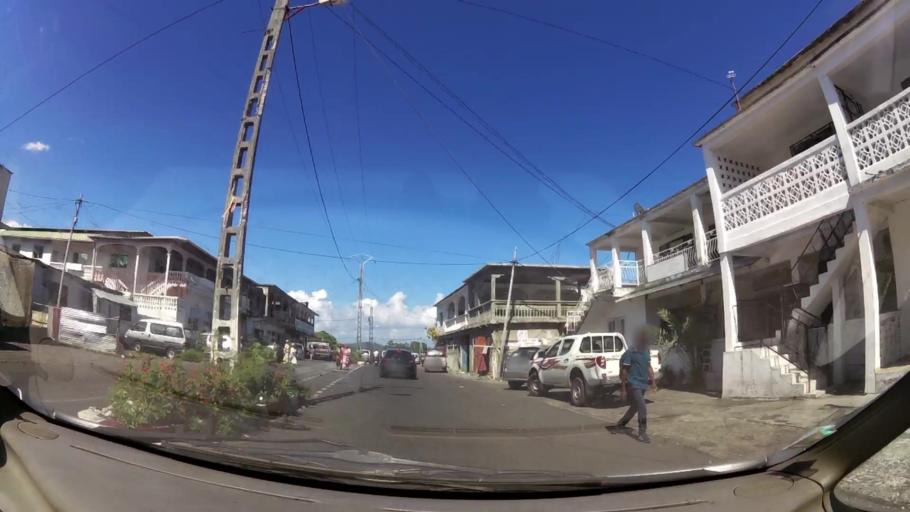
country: KM
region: Grande Comore
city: Moroni
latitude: -11.6974
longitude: 43.2566
